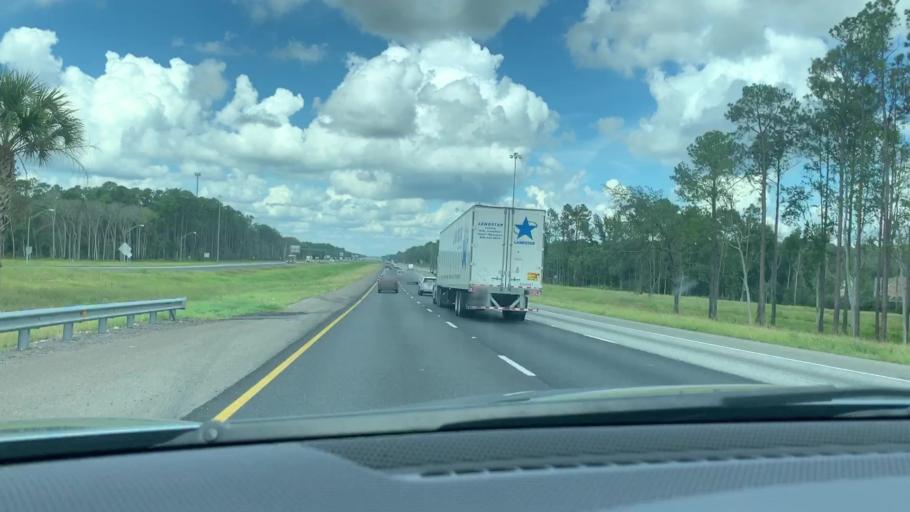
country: US
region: Georgia
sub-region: Camden County
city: Kingsland
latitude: 30.7925
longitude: -81.6591
